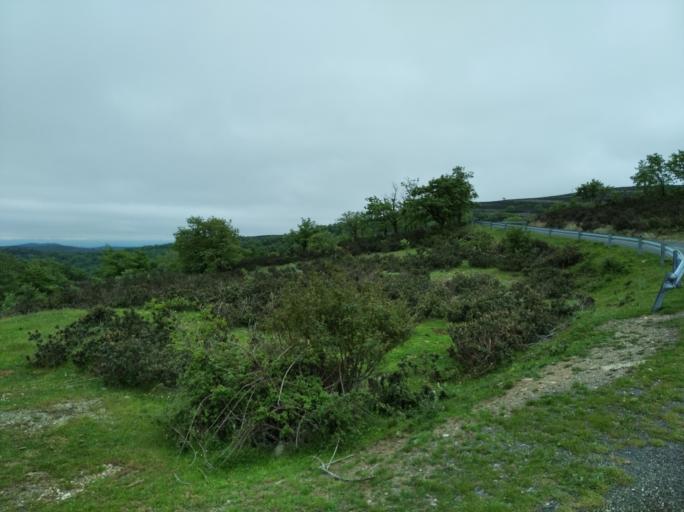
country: ES
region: La Rioja
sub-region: Provincia de La Rioja
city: Robres del Castillo
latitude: 42.2582
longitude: -2.3568
